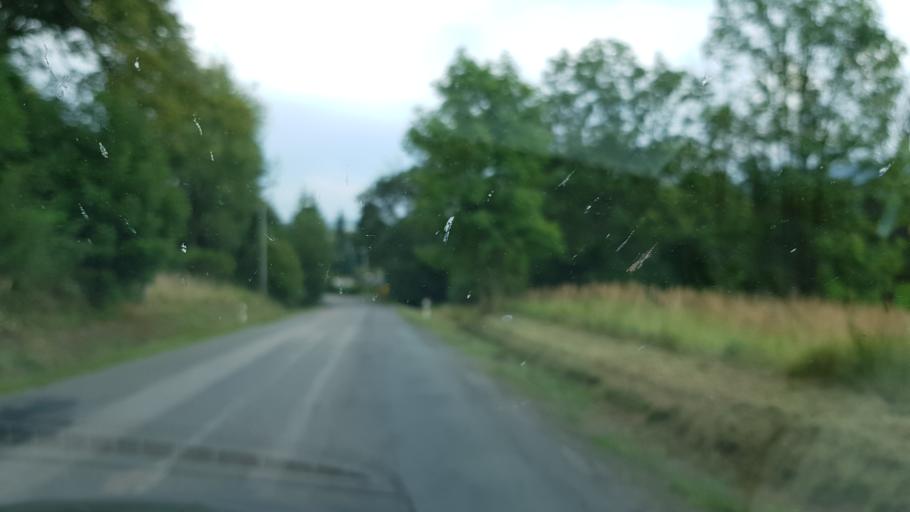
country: CZ
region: Pardubicky
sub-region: Okres Usti nad Orlici
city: Kraliky
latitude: 50.1007
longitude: 16.8041
